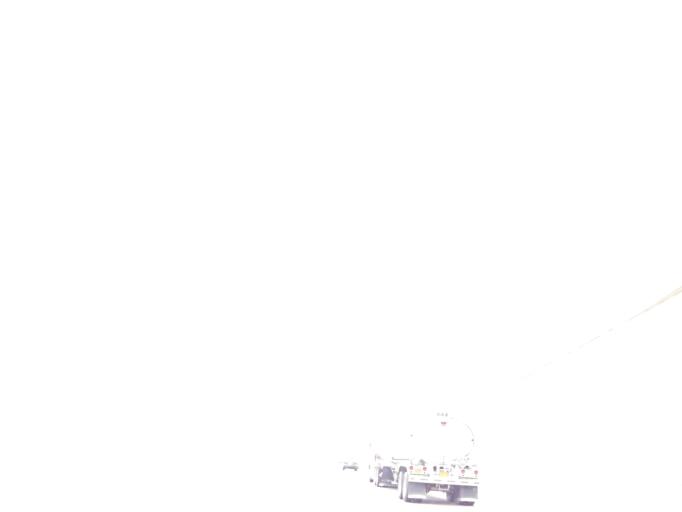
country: US
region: Minnesota
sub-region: Washington County
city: Newport
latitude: 44.8717
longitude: -93.0003
